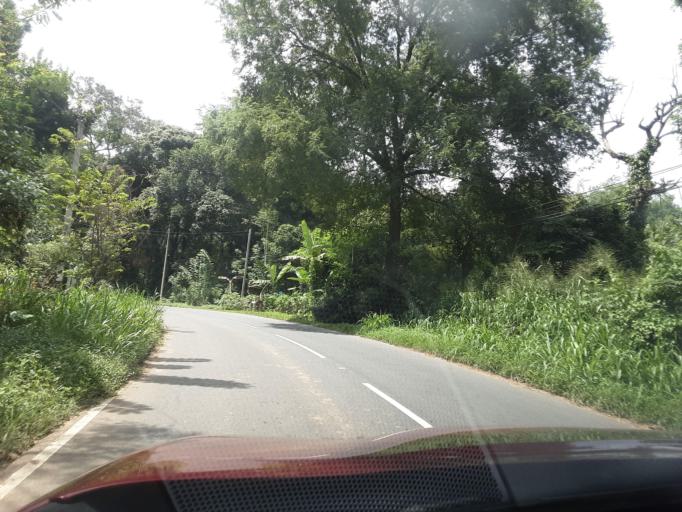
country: LK
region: Uva
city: Monaragala
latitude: 6.8947
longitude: 81.2565
